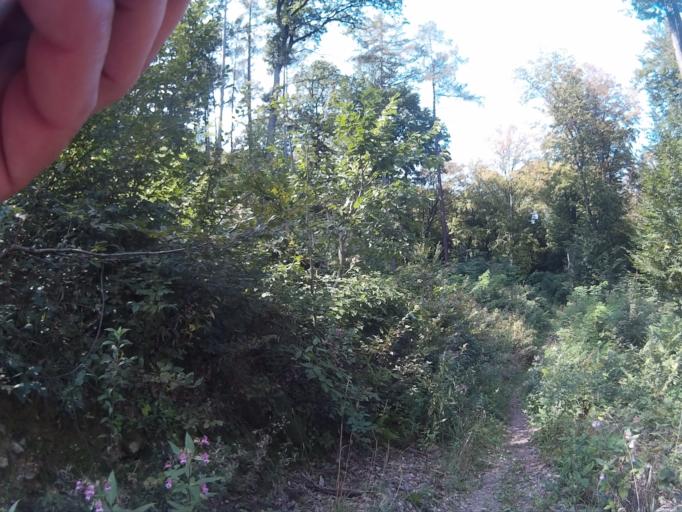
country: HU
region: Vas
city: Koszeg
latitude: 47.4027
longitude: 16.5266
